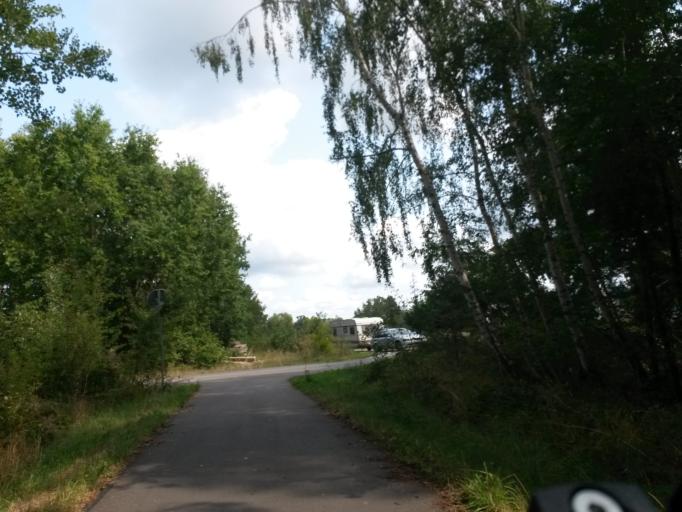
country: DE
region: Saxony-Anhalt
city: Klietz
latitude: 52.6630
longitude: 12.0603
